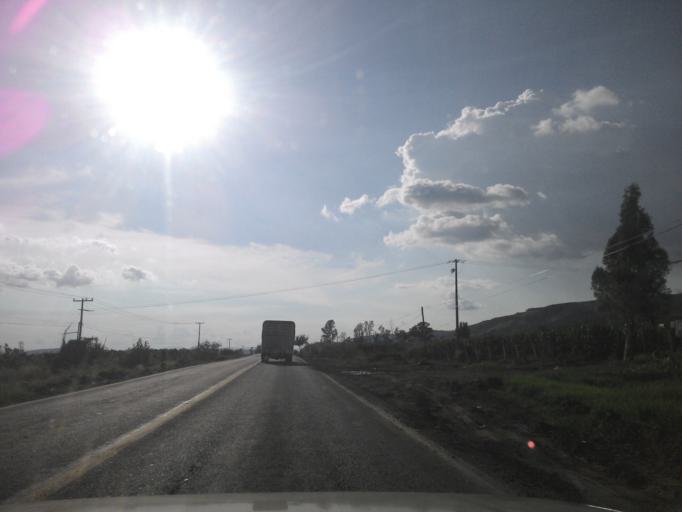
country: MX
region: Jalisco
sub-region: Atotonilco el Alto
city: Vistas del Maguey [Fraccionamiento]
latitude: 20.5402
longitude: -102.5569
